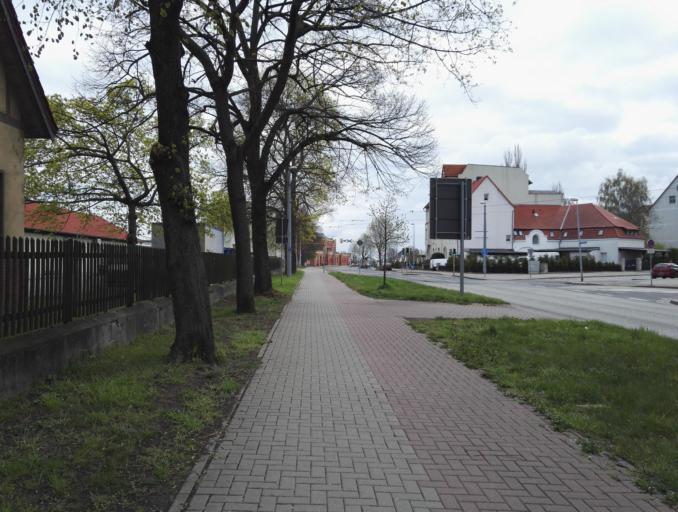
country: DE
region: Saxony-Anhalt
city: Halberstadt
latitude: 51.8993
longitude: 11.0697
